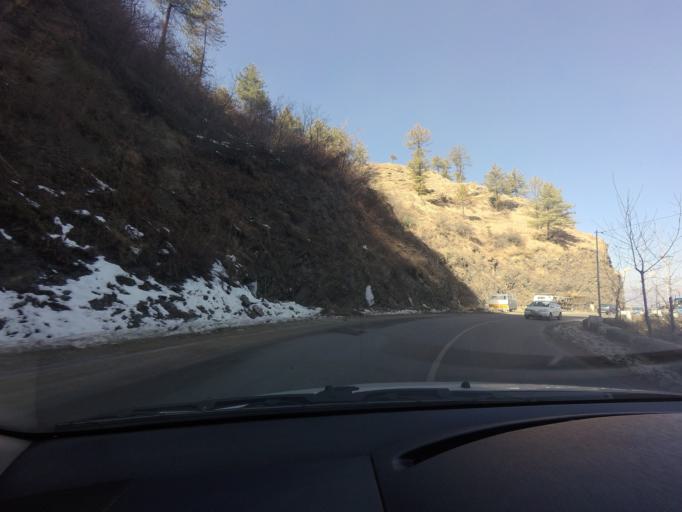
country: IN
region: Himachal Pradesh
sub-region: Shimla
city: Shimla
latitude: 31.1068
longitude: 77.2003
